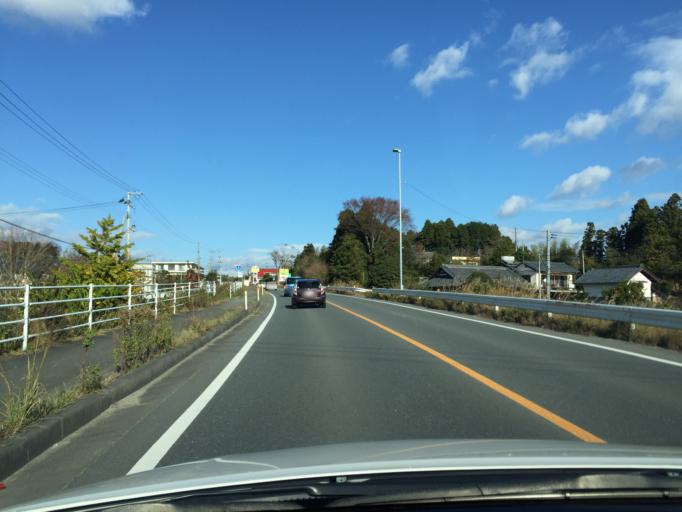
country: JP
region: Fukushima
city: Iwaki
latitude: 37.2263
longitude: 141.0025
